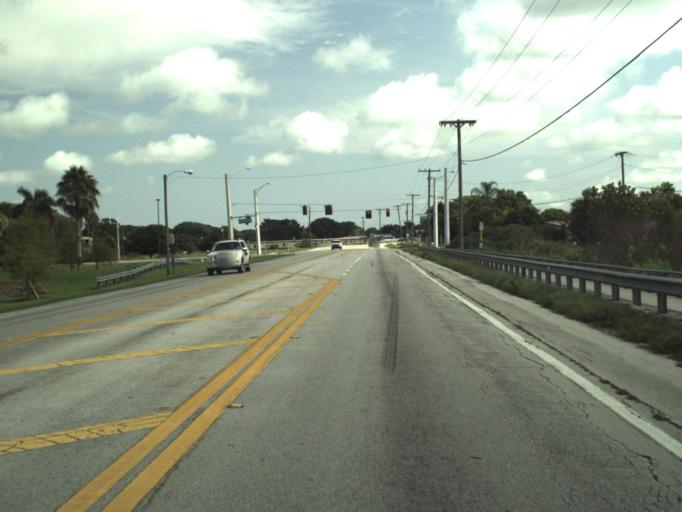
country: US
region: Florida
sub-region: Palm Beach County
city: Belle Glade Camp
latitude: 26.6754
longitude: -80.6866
